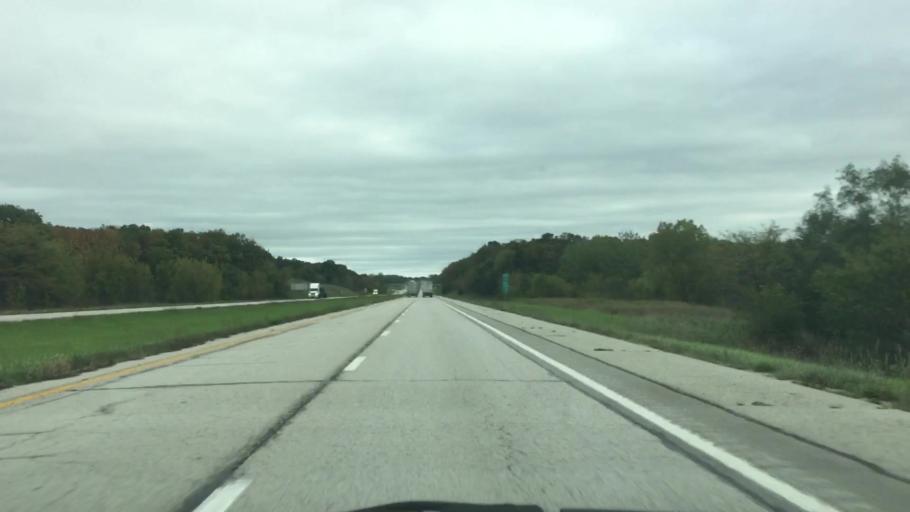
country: US
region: Missouri
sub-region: Harrison County
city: Bethany
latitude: 40.0932
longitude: -94.0822
